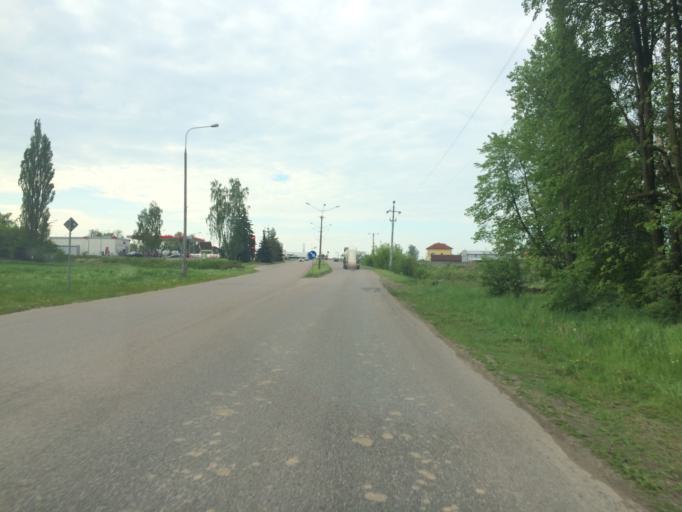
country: PL
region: Masovian Voivodeship
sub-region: Powiat mlawski
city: Mlawa
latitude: 53.0965
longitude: 20.3734
